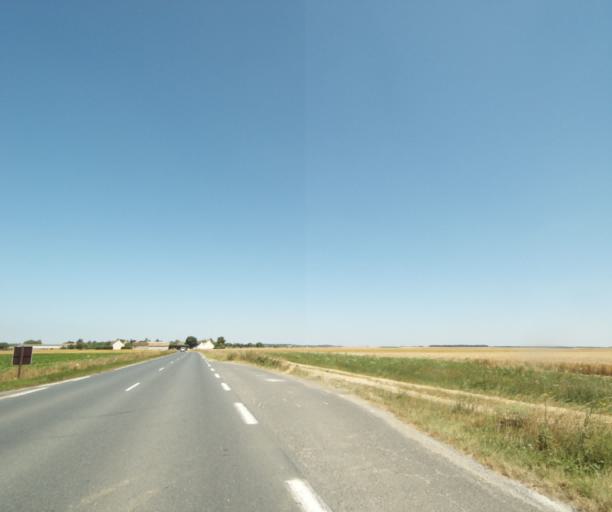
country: FR
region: Ile-de-France
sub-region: Departement de Seine-et-Marne
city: La Chapelle-la-Reine
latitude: 48.3100
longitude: 2.5412
